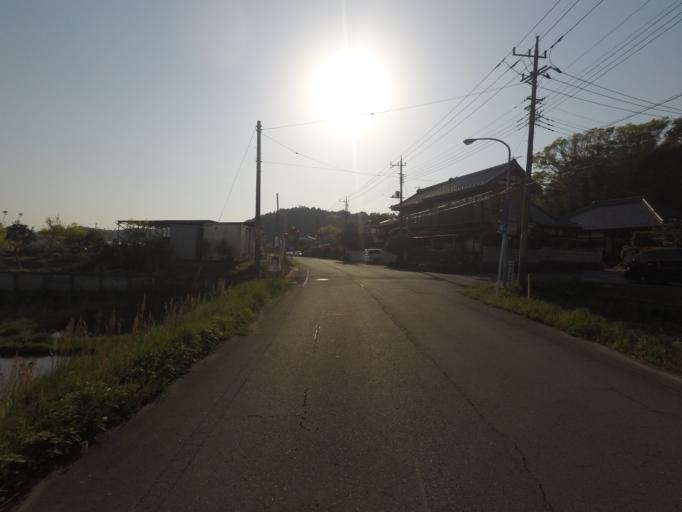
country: JP
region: Ibaraki
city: Ami
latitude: 36.0714
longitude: 140.3039
